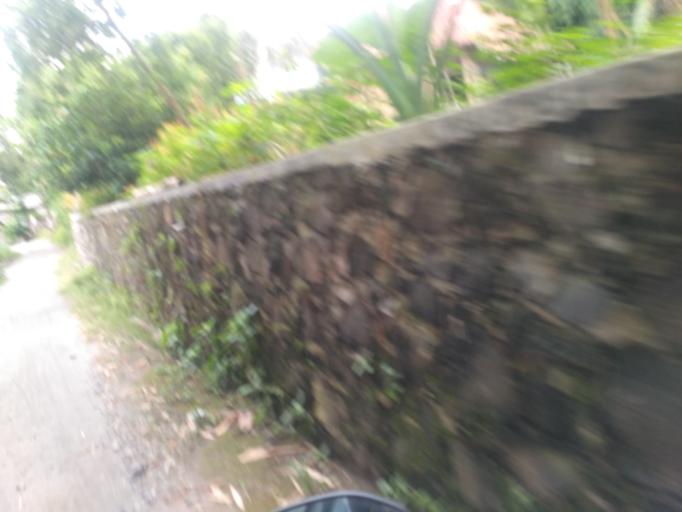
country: ID
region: Daerah Istimewa Yogyakarta
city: Yogyakarta
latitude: -7.7655
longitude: 110.3521
